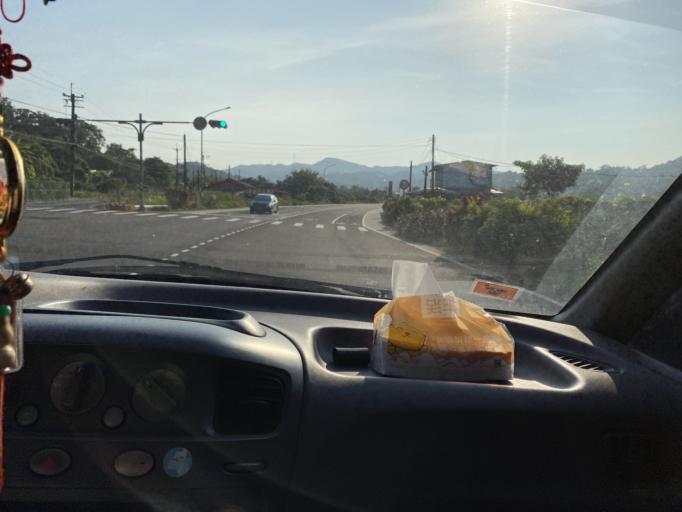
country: TW
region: Taiwan
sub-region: Keelung
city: Keelung
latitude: 25.0359
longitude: 121.8520
